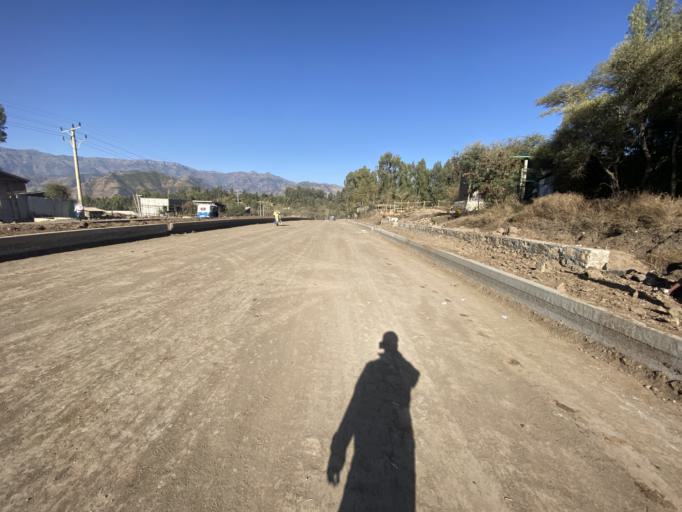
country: ET
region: Amhara
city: Robit
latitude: 11.8277
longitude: 39.5700
